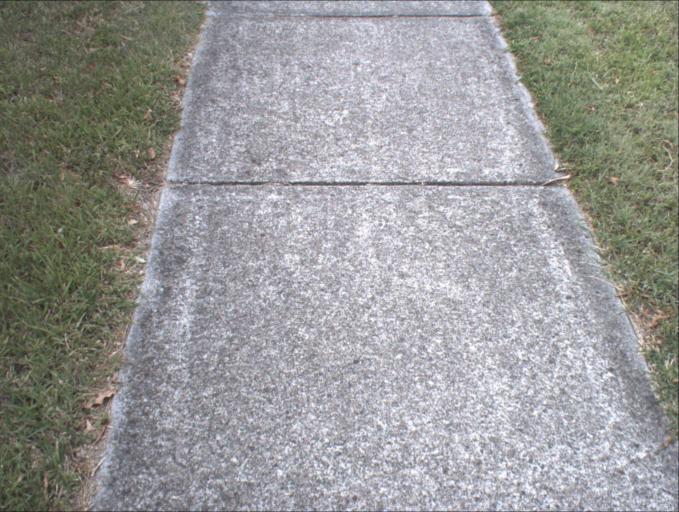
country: AU
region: Queensland
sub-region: Logan
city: Woodridge
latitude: -27.6095
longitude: 153.1027
